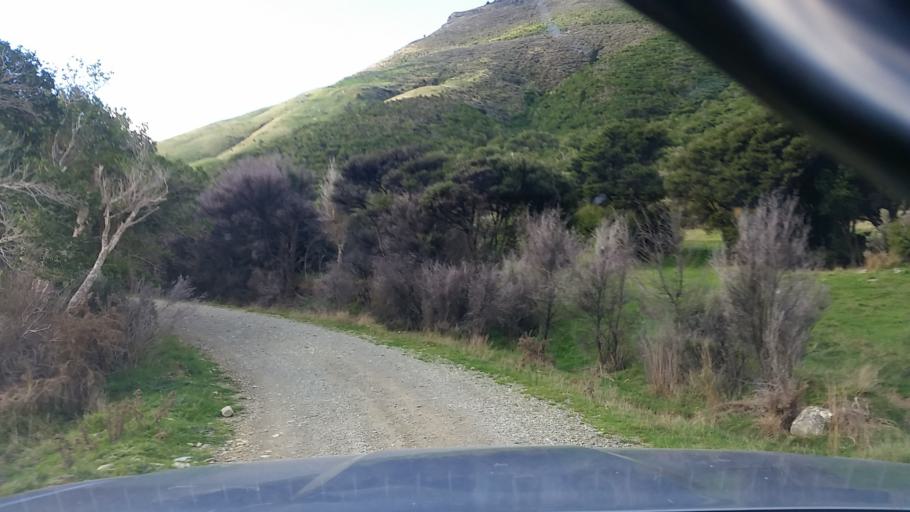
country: NZ
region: Marlborough
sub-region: Marlborough District
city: Picton
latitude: -41.0548
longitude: 174.1097
